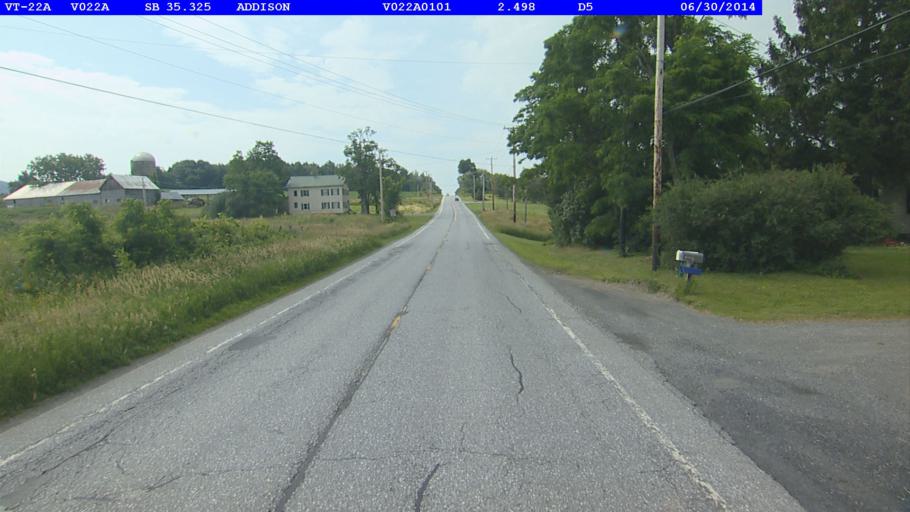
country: US
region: Vermont
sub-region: Addison County
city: Vergennes
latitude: 44.0654
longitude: -73.3038
